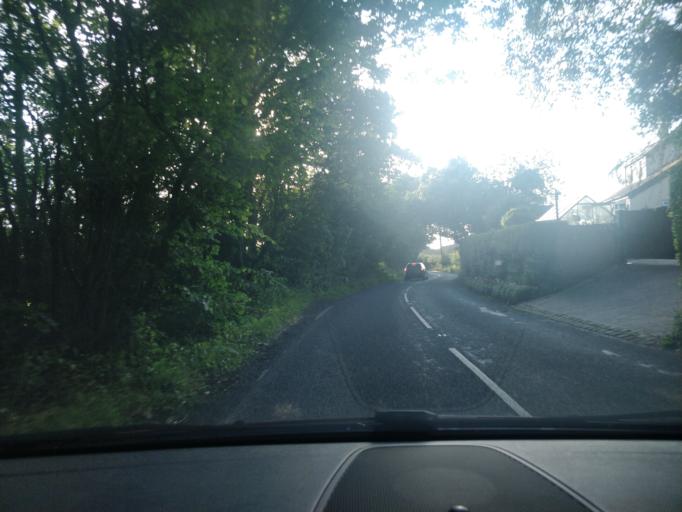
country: GB
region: England
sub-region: Lancashire
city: Skelmersdale
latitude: 53.5646
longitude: -2.7571
